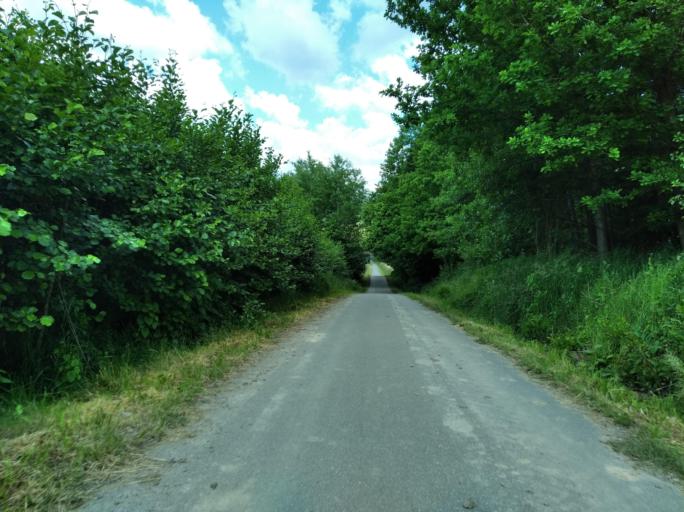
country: PL
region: Subcarpathian Voivodeship
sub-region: Powiat strzyzowski
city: Jawornik
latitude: 49.7835
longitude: 21.8671
